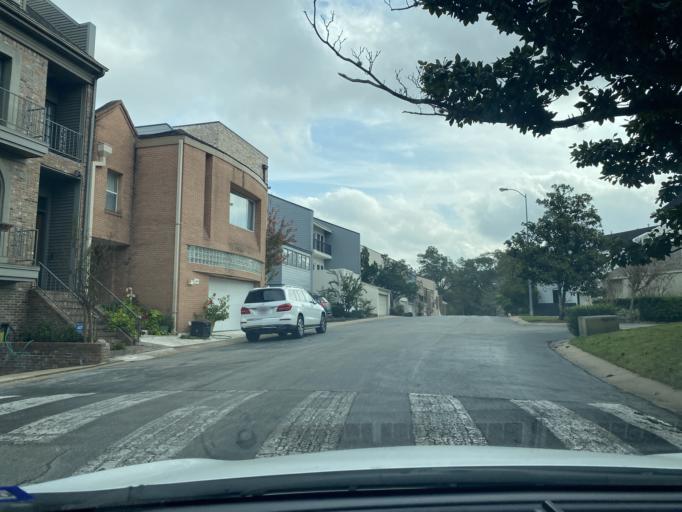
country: US
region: Texas
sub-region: Harris County
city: Hunters Creek Village
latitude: 29.7686
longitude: -95.4675
